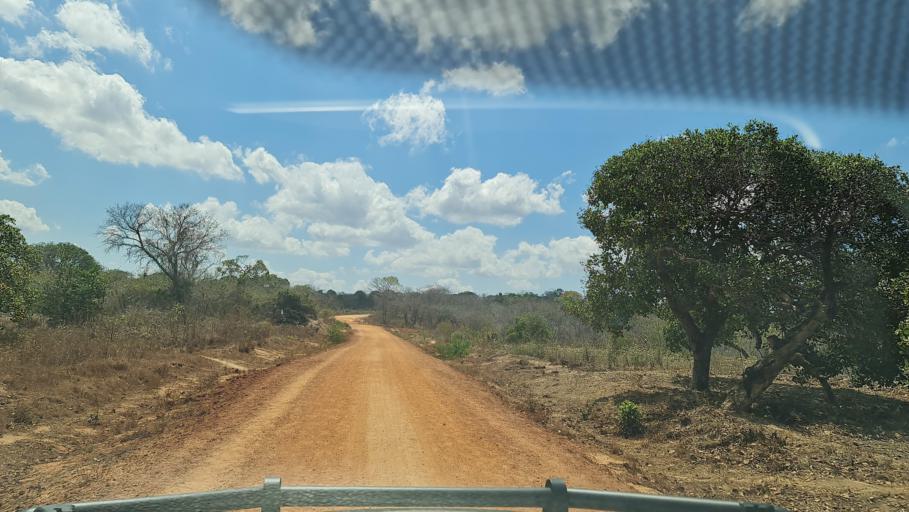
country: MZ
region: Nampula
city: Nacala
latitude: -14.1691
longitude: 40.2520
